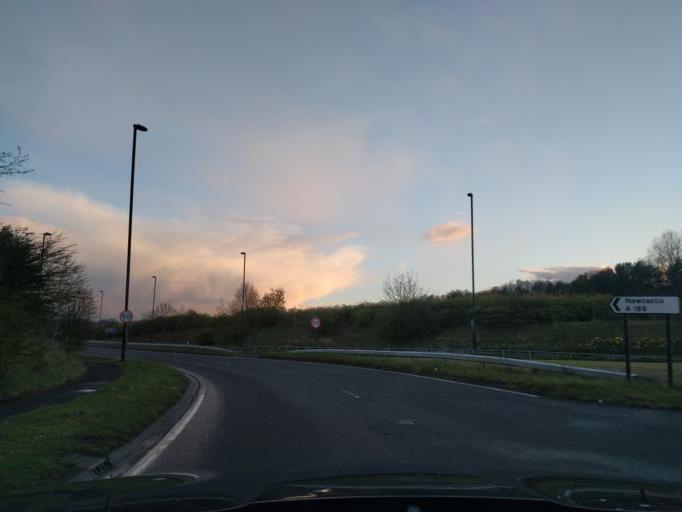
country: GB
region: England
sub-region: Newcastle upon Tyne
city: Gosforth
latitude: 55.0392
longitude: -1.5921
